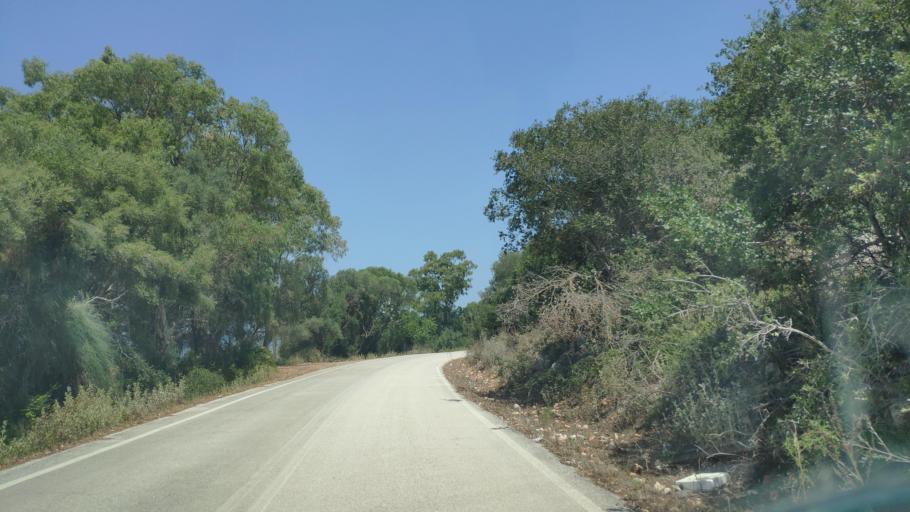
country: GR
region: Epirus
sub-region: Nomos Artas
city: Aneza
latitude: 39.0339
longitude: 20.8602
